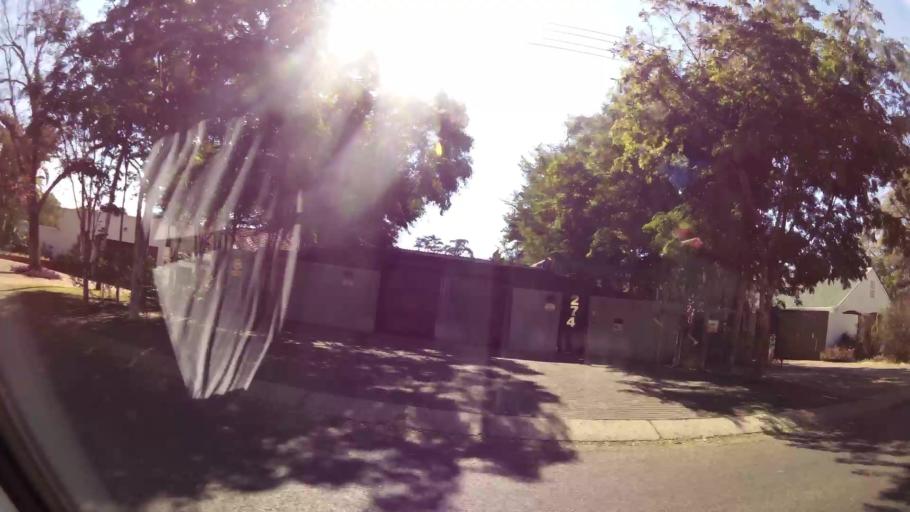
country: ZA
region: Gauteng
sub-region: City of Tshwane Metropolitan Municipality
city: Pretoria
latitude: -25.7699
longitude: 28.2418
